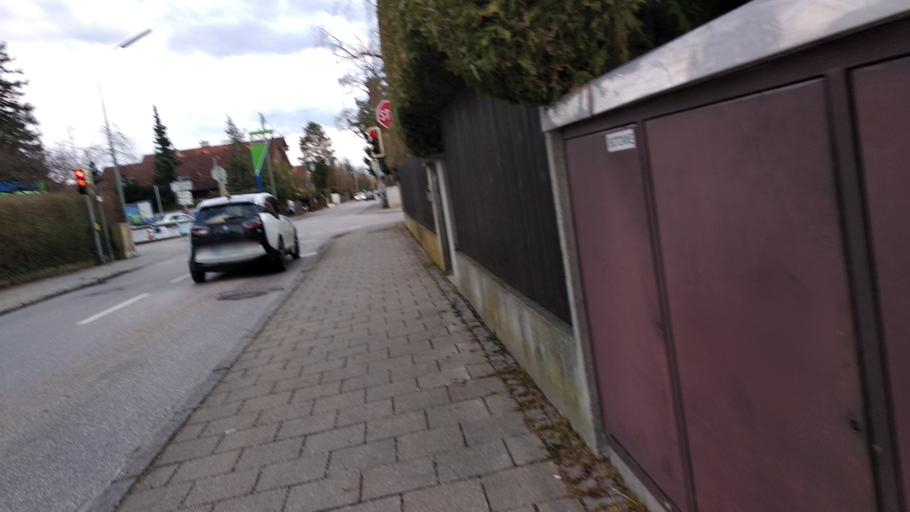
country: DE
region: Bavaria
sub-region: Upper Bavaria
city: Ottobrunn
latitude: 48.0750
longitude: 11.6769
